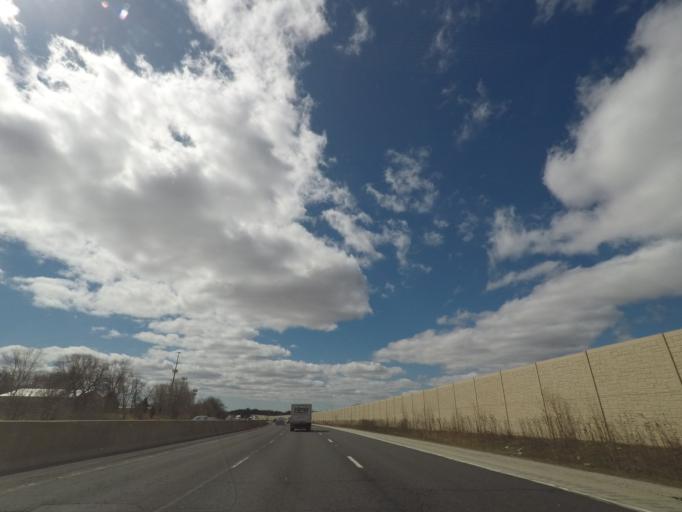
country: US
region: Illinois
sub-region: Will County
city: Crystal Lawns
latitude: 41.5718
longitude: -88.1807
